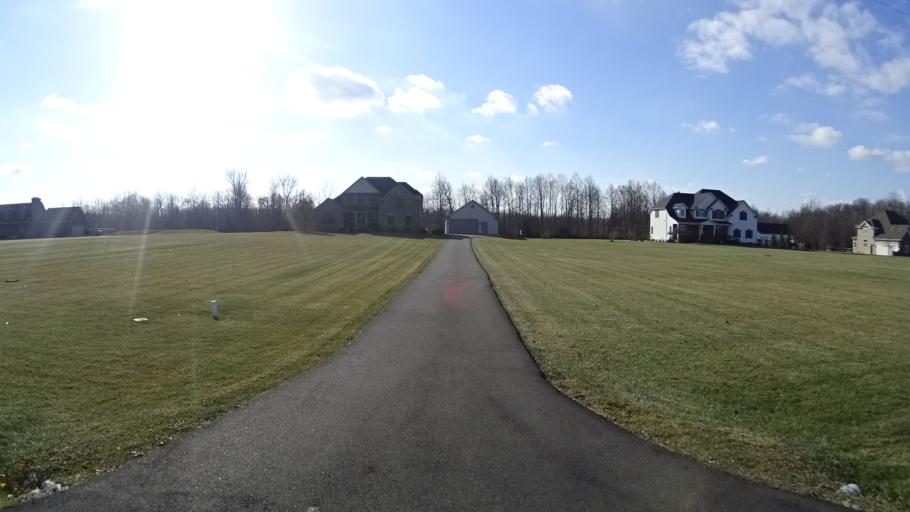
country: US
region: Ohio
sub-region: Lorain County
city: Wellington
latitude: 41.2100
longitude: -82.2242
